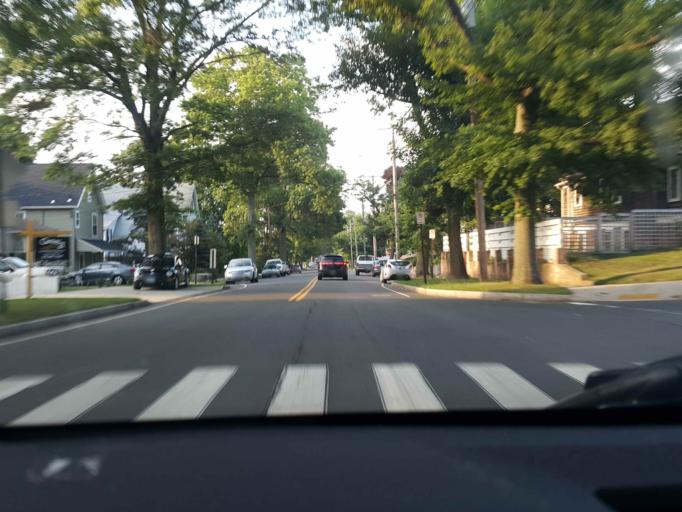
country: US
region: Connecticut
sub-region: New Haven County
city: East Haven
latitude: 41.2808
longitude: -72.8976
